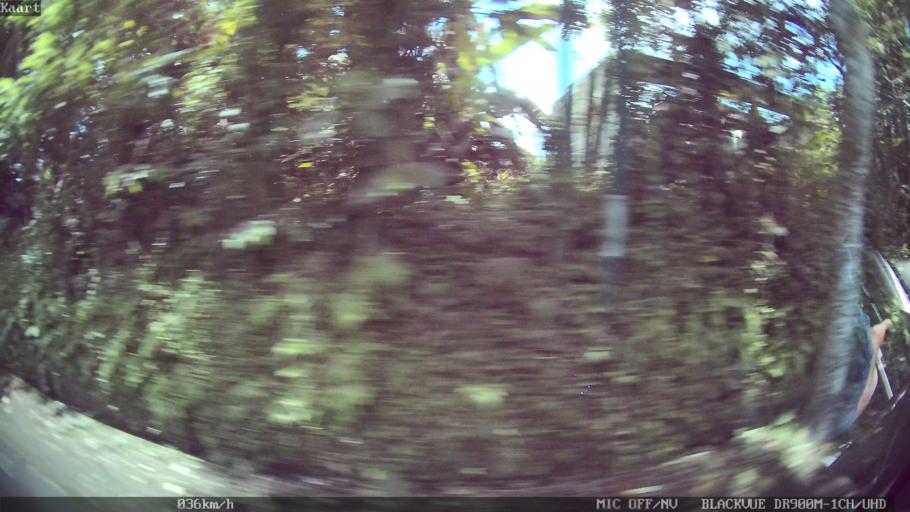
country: ID
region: Bali
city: Klungkung
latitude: -8.5212
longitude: 115.3801
